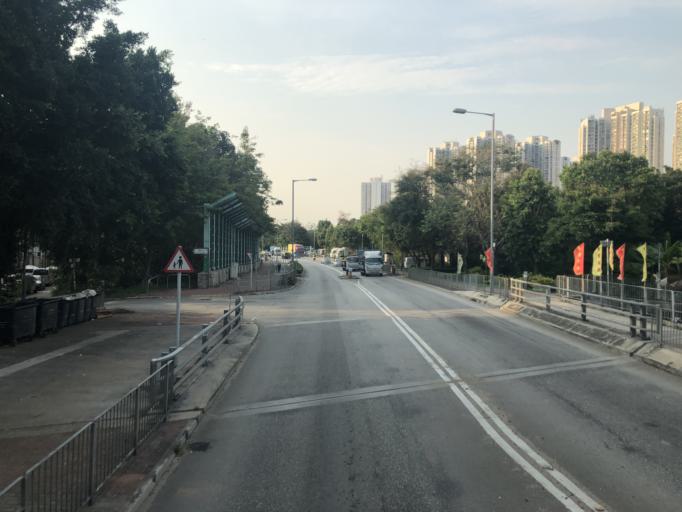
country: HK
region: Yuen Long
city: Yuen Long Kau Hui
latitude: 22.4516
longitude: 113.9949
